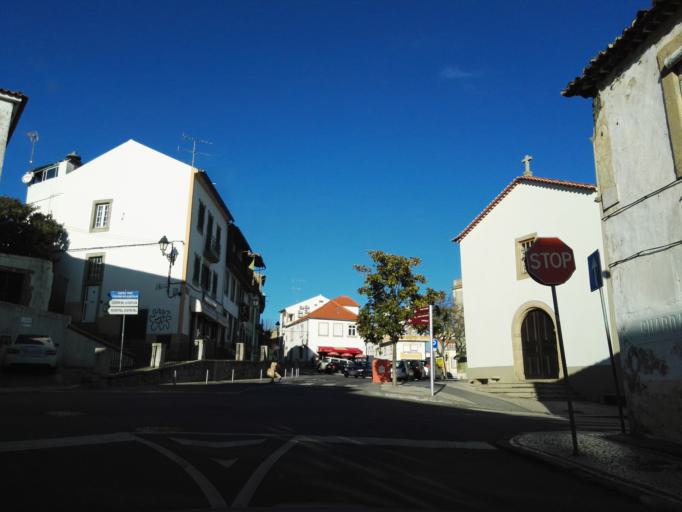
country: PT
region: Castelo Branco
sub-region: Castelo Branco
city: Castelo Branco
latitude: 39.8223
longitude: -7.4953
